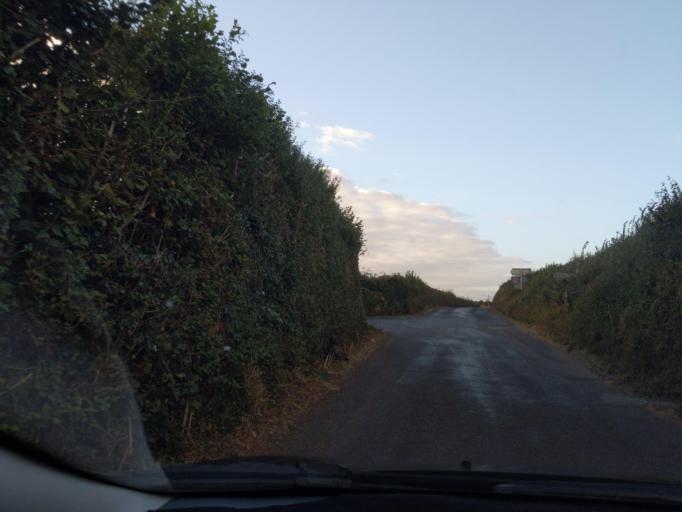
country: GB
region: England
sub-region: Devon
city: Salcombe
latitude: 50.2384
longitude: -3.8211
